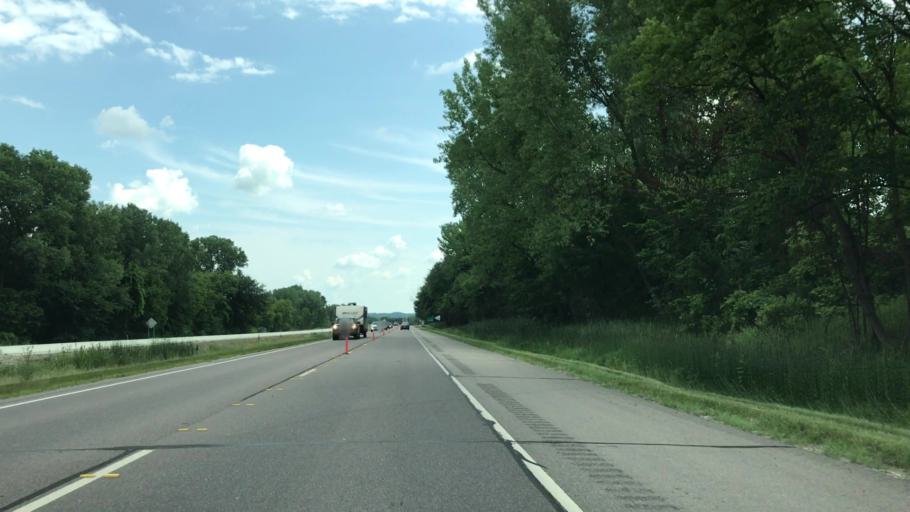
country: US
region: Minnesota
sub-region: Nicollet County
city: Saint Peter
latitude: 44.3588
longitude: -93.9578
